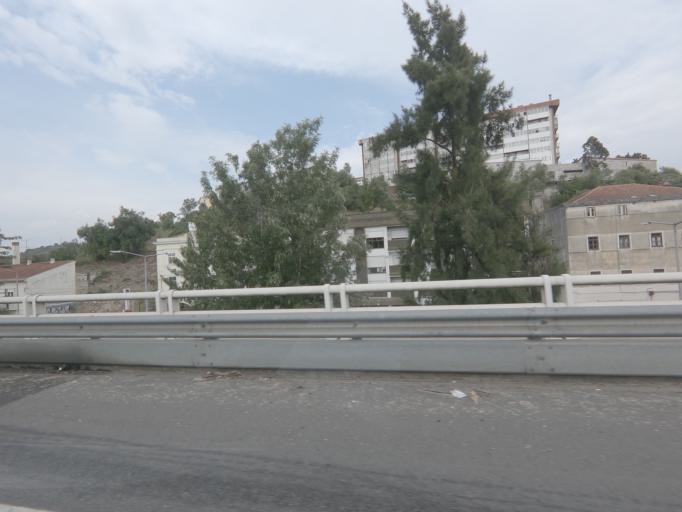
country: PT
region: Coimbra
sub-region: Coimbra
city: Coimbra
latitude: 40.2219
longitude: -8.4395
